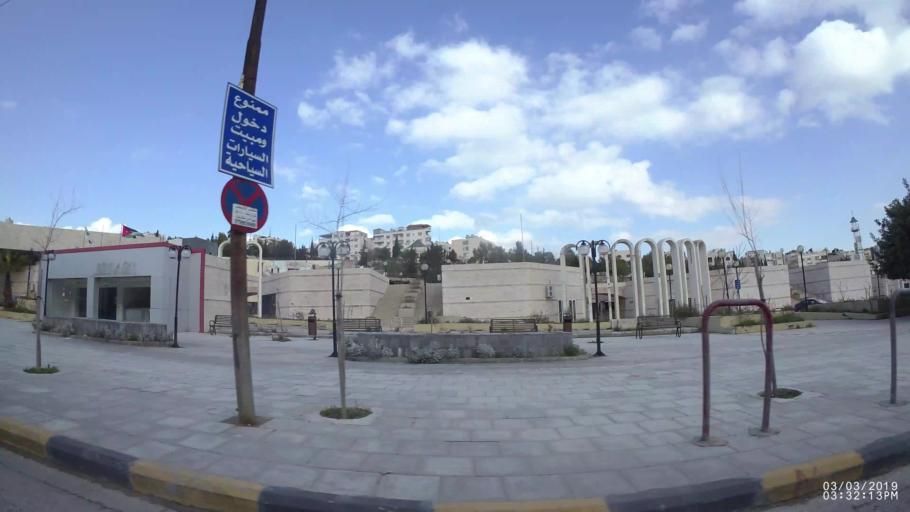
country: JO
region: Amman
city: Amman
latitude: 31.9690
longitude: 35.8865
